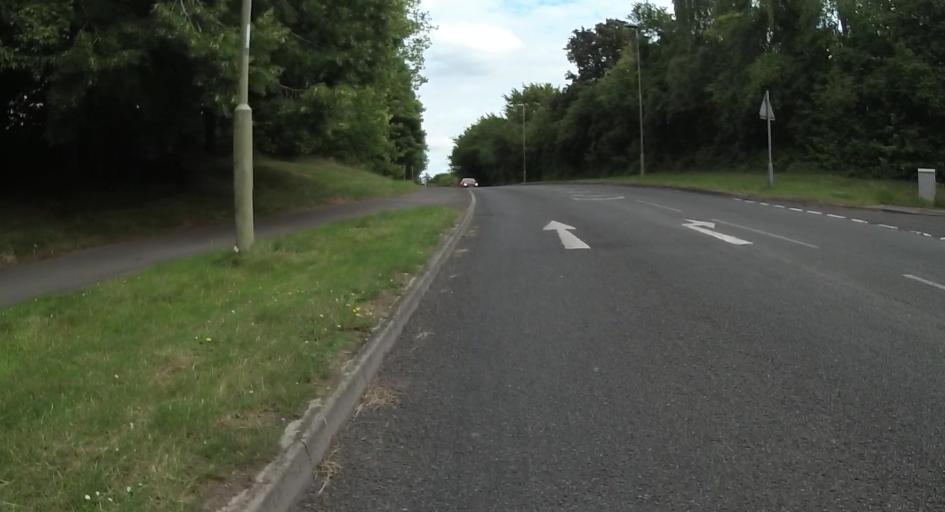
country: GB
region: England
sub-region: Hampshire
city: Old Basing
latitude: 51.2755
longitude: -1.0590
